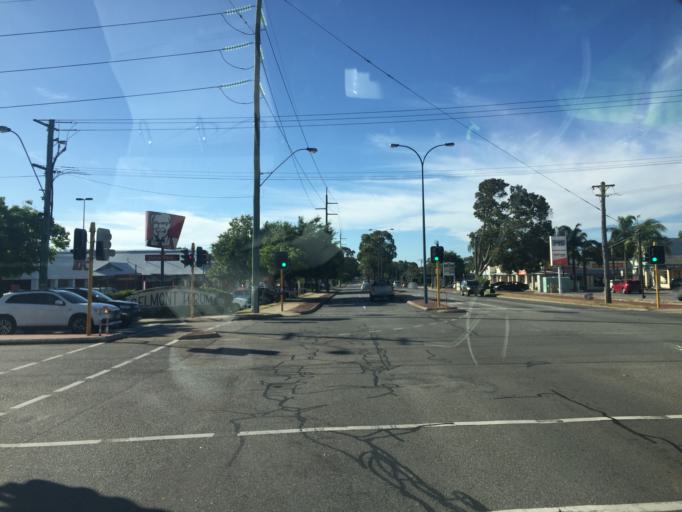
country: AU
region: Western Australia
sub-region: Belmont
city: Kewdale
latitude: -31.9644
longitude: 115.9385
